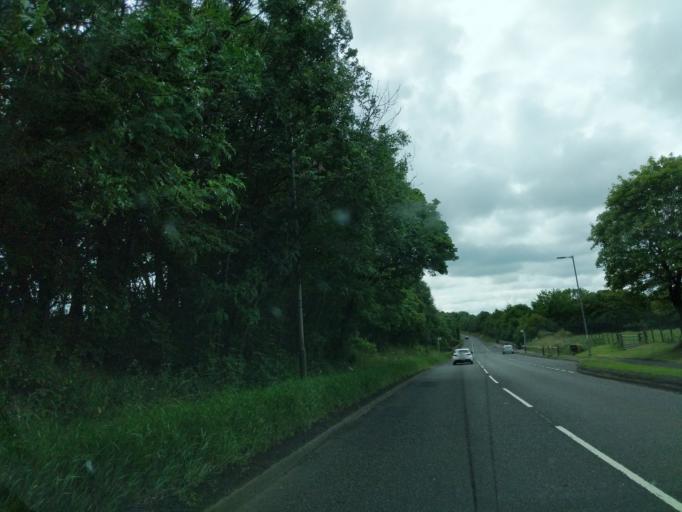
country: GB
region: Scotland
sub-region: South Lanarkshire
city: Larkhall
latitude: 55.7068
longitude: -3.9640
